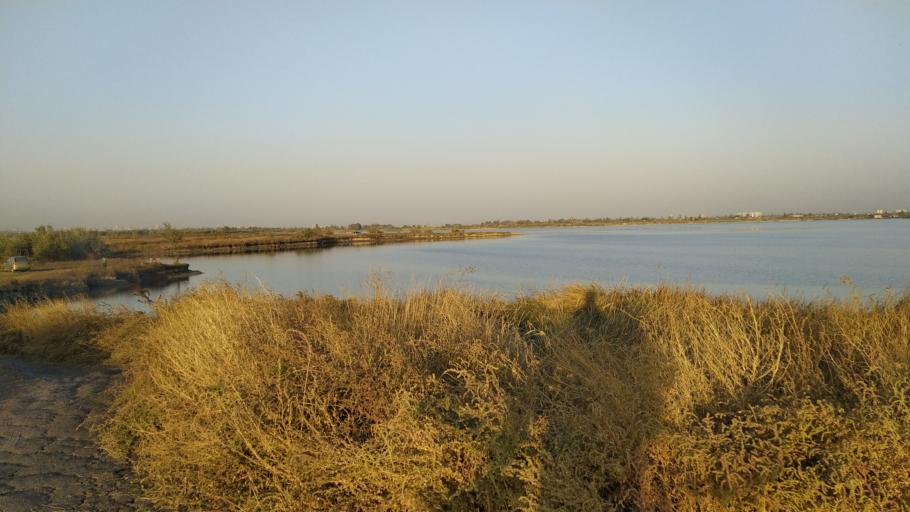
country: RU
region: Rostov
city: Bataysk
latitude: 47.1424
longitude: 39.6445
